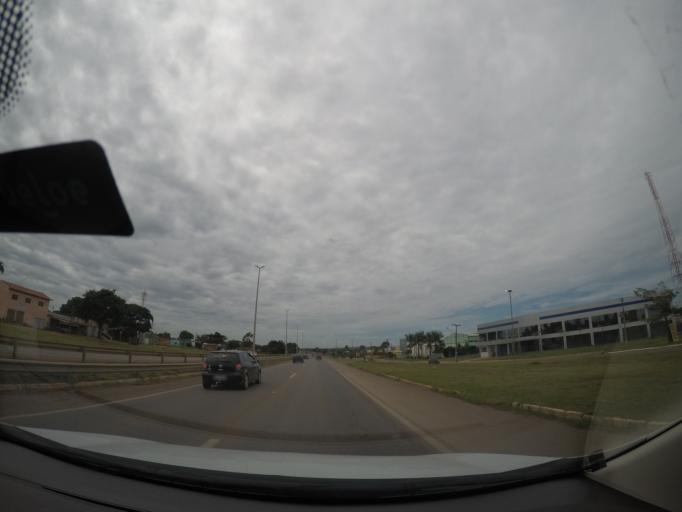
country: BR
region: Goias
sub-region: Goianira
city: Goianira
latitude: -16.5365
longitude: -49.4059
